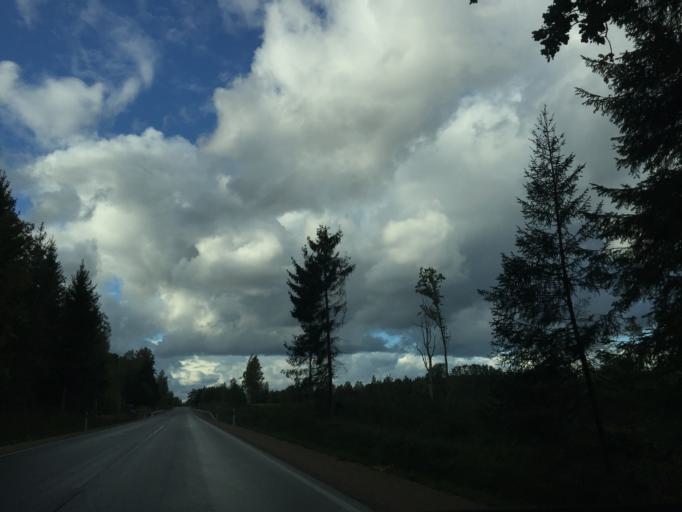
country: LV
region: Ligatne
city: Ligatne
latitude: 57.1681
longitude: 25.0465
